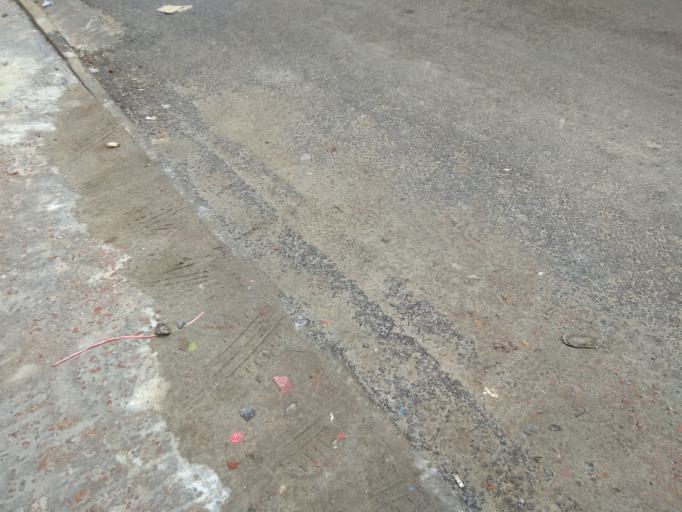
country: BD
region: Dhaka
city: Azimpur
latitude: 23.8034
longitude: 90.3565
